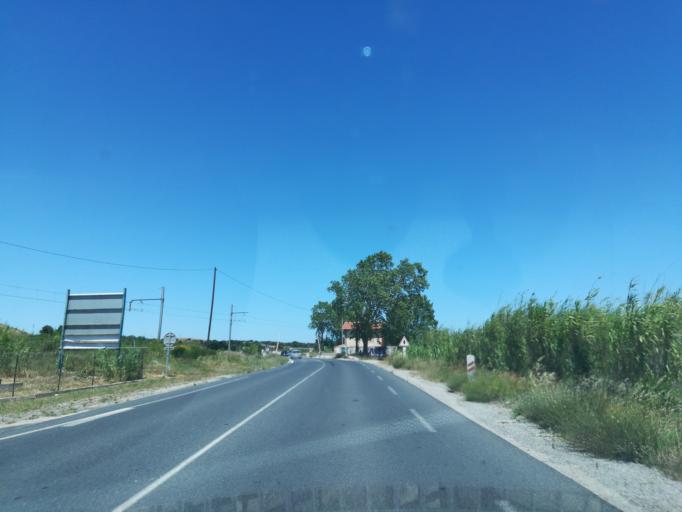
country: FR
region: Languedoc-Roussillon
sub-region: Departement des Pyrenees-Orientales
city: el Volo
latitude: 42.5410
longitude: 2.8482
